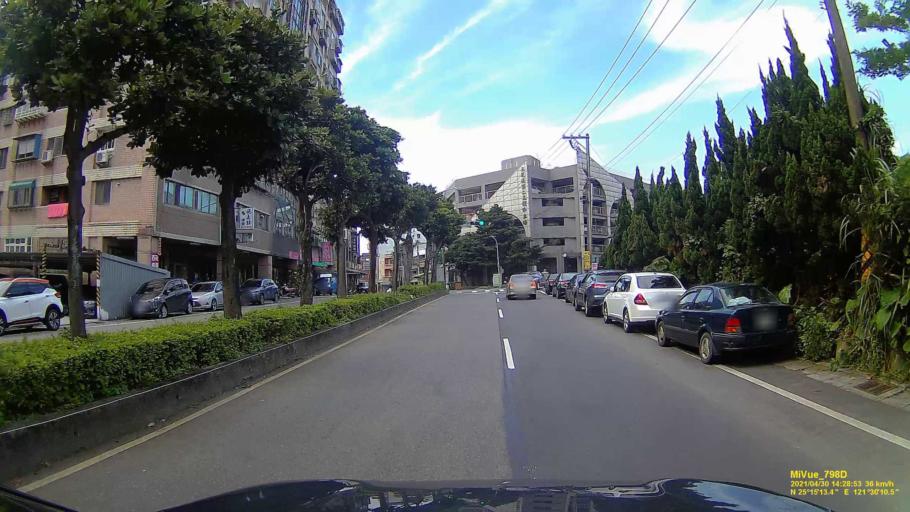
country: TW
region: Taipei
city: Taipei
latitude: 25.2539
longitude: 121.5029
